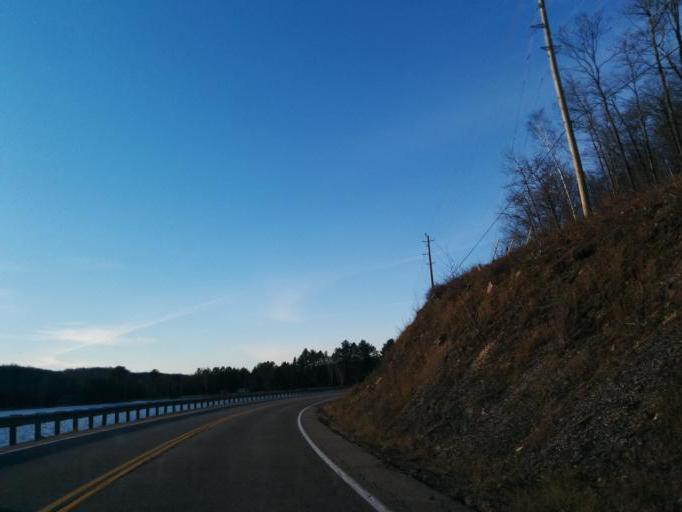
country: CA
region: Ontario
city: Bancroft
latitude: 45.0232
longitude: -78.3799
